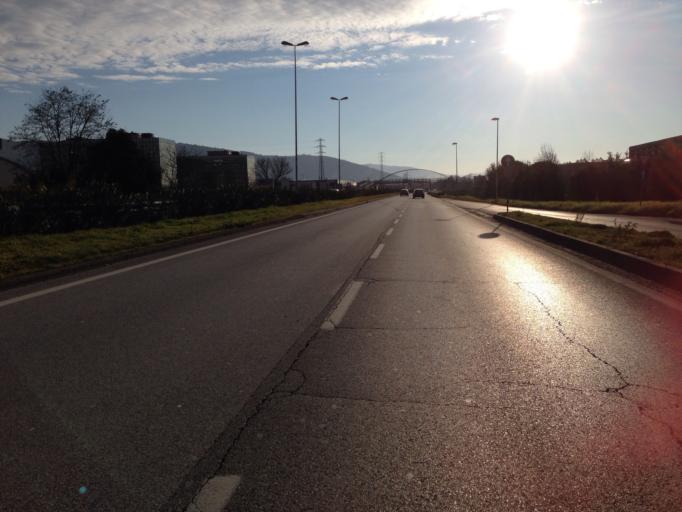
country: IT
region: Tuscany
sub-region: Provincia di Prato
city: Prato
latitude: 43.8779
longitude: 11.0680
